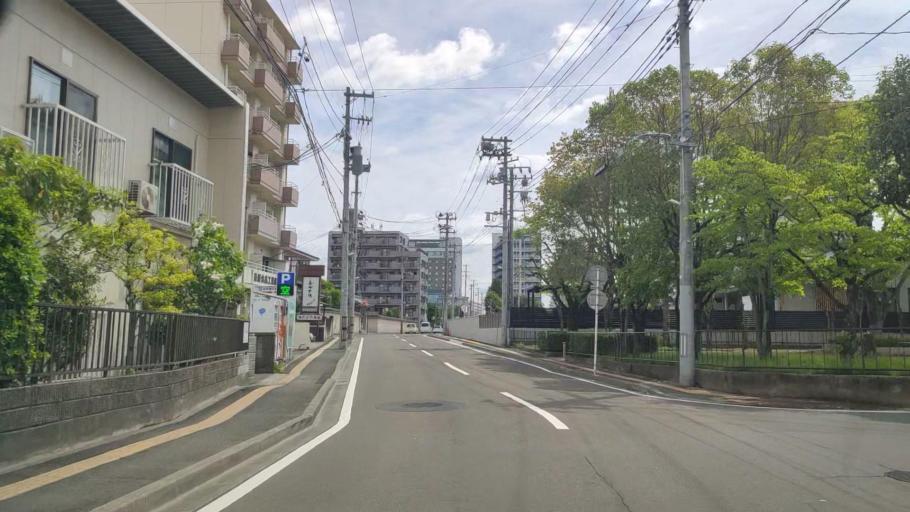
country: JP
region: Miyagi
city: Sendai-shi
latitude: 38.2573
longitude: 140.8870
